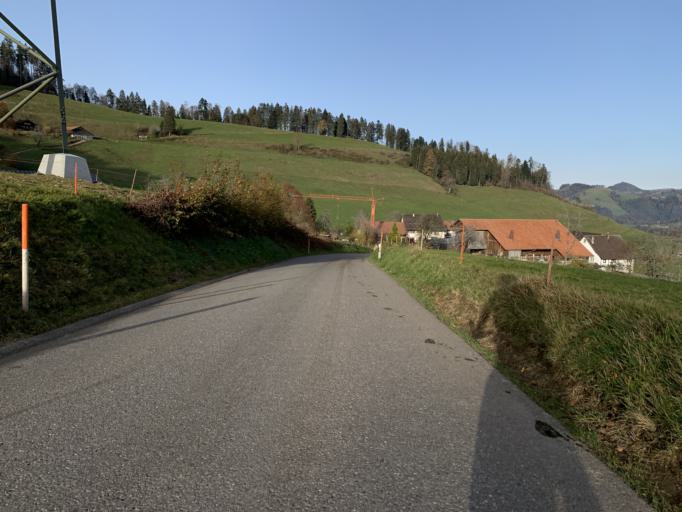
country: CH
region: Zurich
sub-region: Bezirk Hinwil
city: Wald
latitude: 47.3097
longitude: 8.8923
